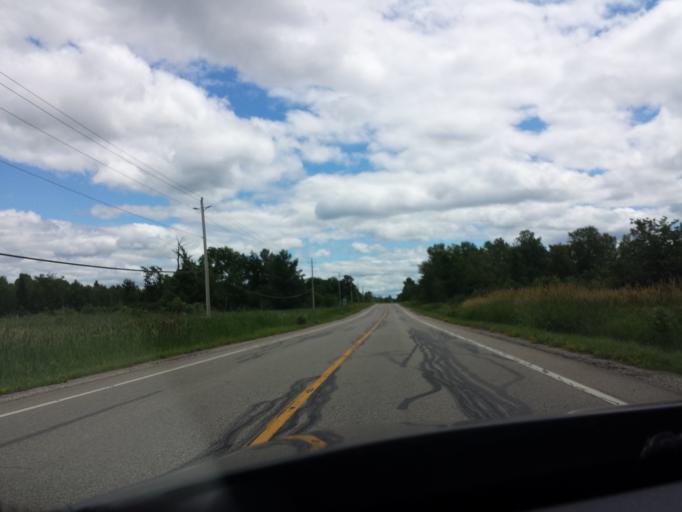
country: CA
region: Ontario
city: Perth
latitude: 44.8471
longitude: -76.2004
